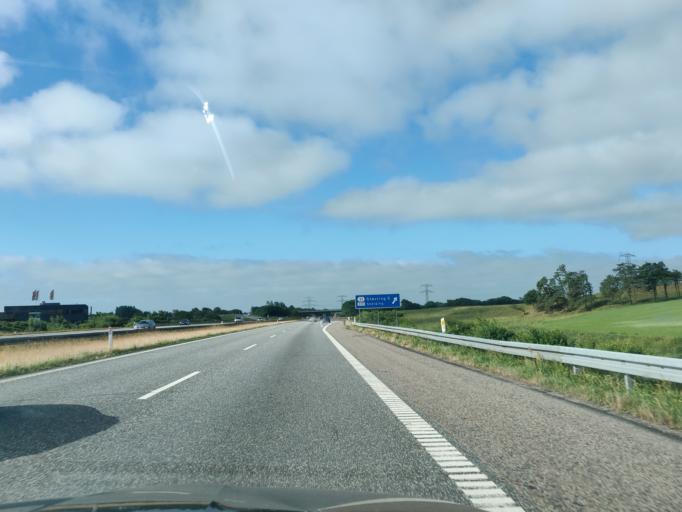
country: DK
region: North Denmark
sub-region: Rebild Kommune
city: Stovring
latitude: 56.8845
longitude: 9.8073
